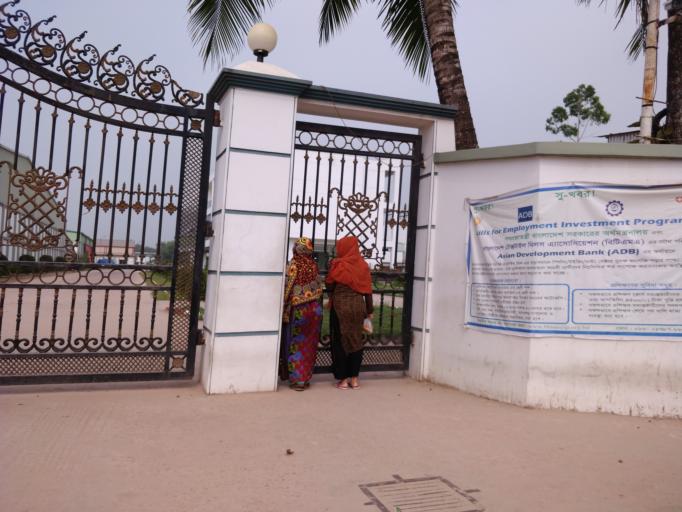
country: BD
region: Sylhet
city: Habiganj
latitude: 24.1720
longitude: 91.3554
